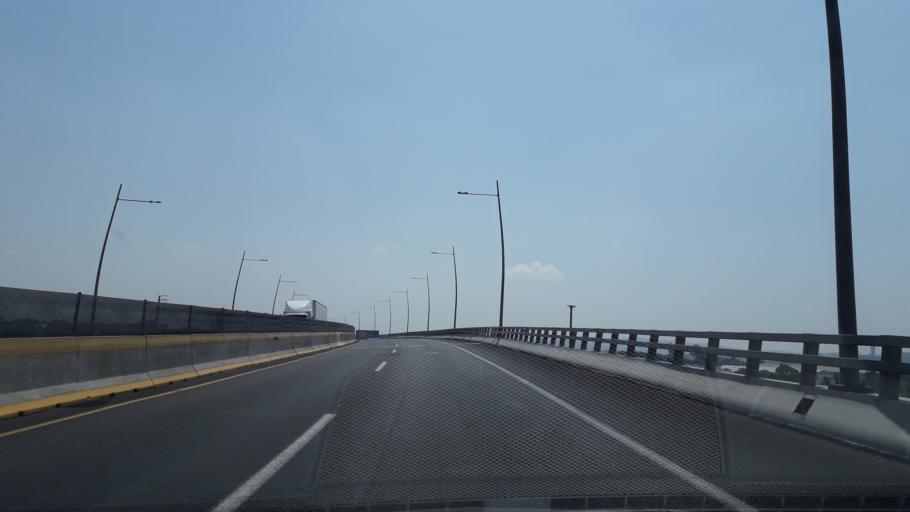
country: MX
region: Puebla
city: Puebla
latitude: 19.0872
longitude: -98.2070
